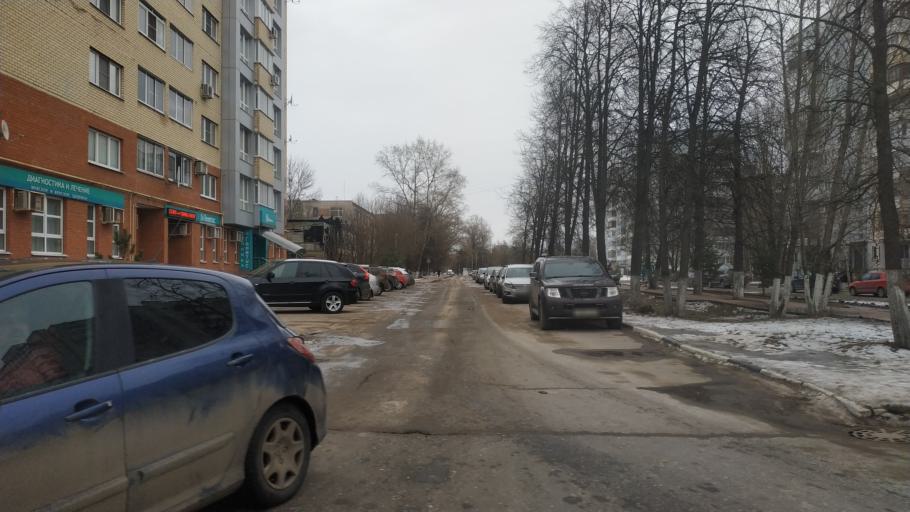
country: RU
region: Tverskaya
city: Tver
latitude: 56.8752
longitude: 35.8909
